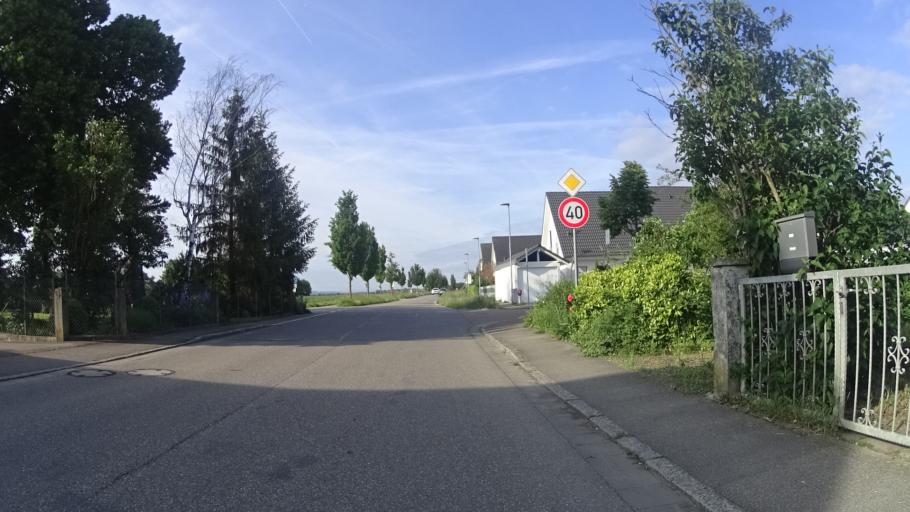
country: DE
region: Baden-Wuerttemberg
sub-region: Freiburg Region
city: Buggingen
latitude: 47.8685
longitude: 7.5890
